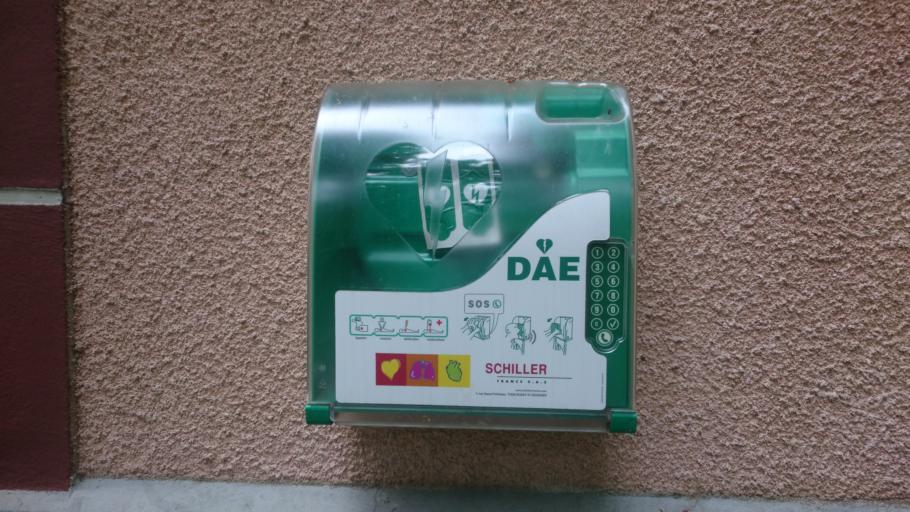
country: FR
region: Ile-de-France
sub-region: Departement du Val-de-Marne
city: Maisons-Alfort
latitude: 48.8168
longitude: 2.4345
